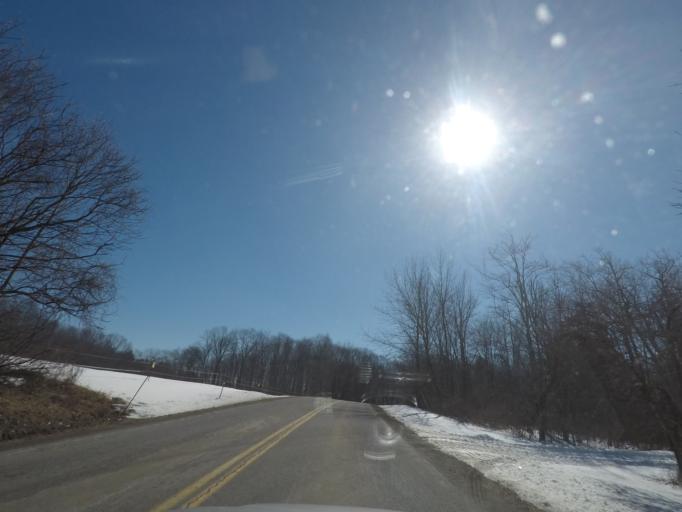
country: US
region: New York
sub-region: Saratoga County
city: Stillwater
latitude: 43.0296
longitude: -73.6705
